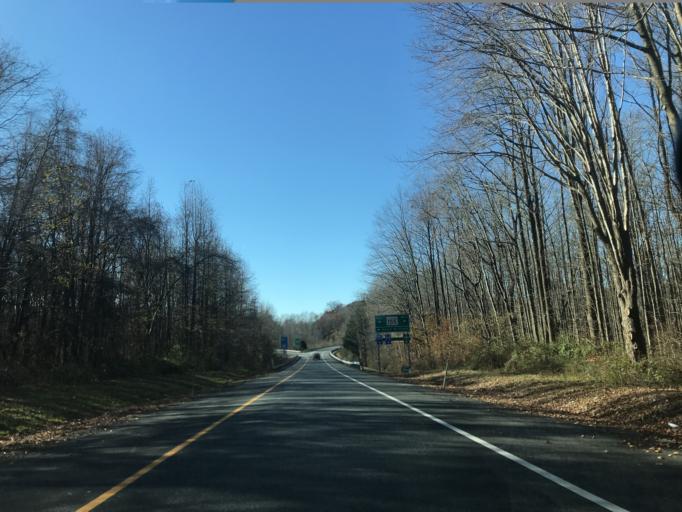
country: US
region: Maryland
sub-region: Harford County
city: Havre de Grace
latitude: 39.5739
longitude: -76.1372
